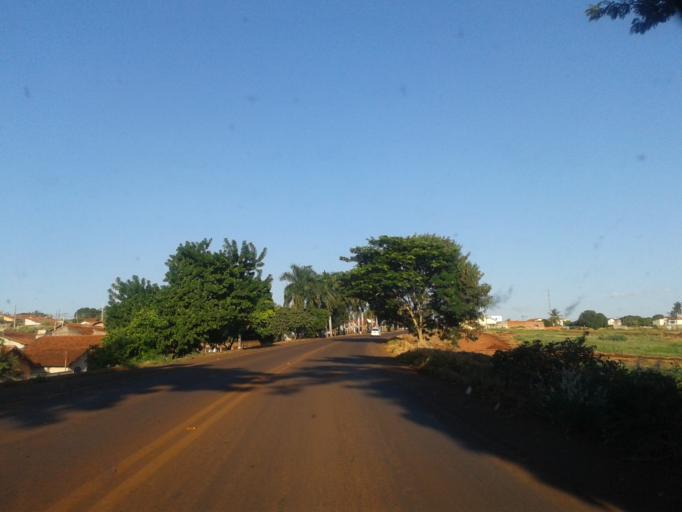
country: BR
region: Minas Gerais
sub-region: Capinopolis
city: Capinopolis
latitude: -18.6866
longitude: -49.5725
